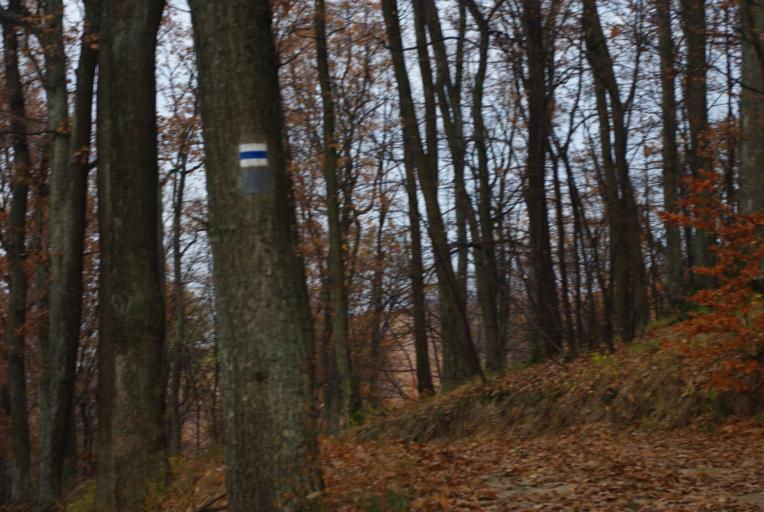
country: HU
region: Borsod-Abauj-Zemplen
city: Satoraljaujhely
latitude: 48.3996
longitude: 21.6196
